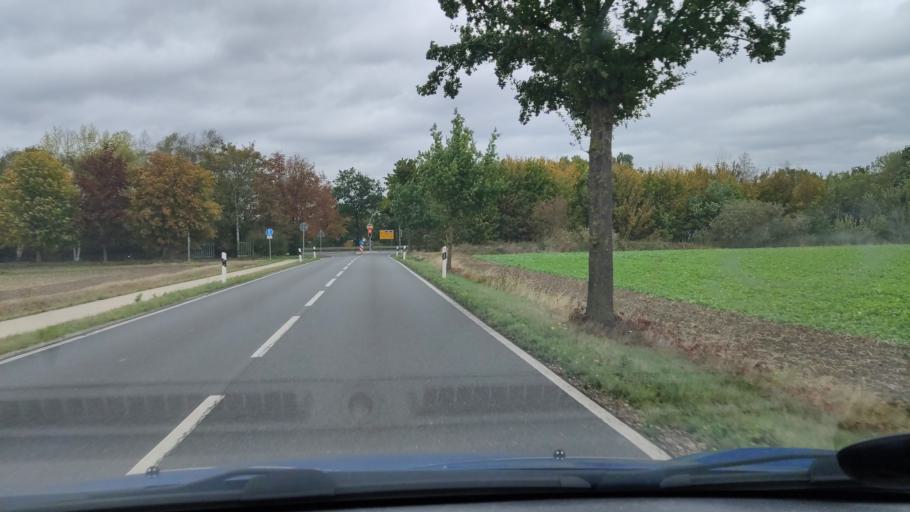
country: DE
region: Lower Saxony
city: Seelze
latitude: 52.3876
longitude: 9.6145
